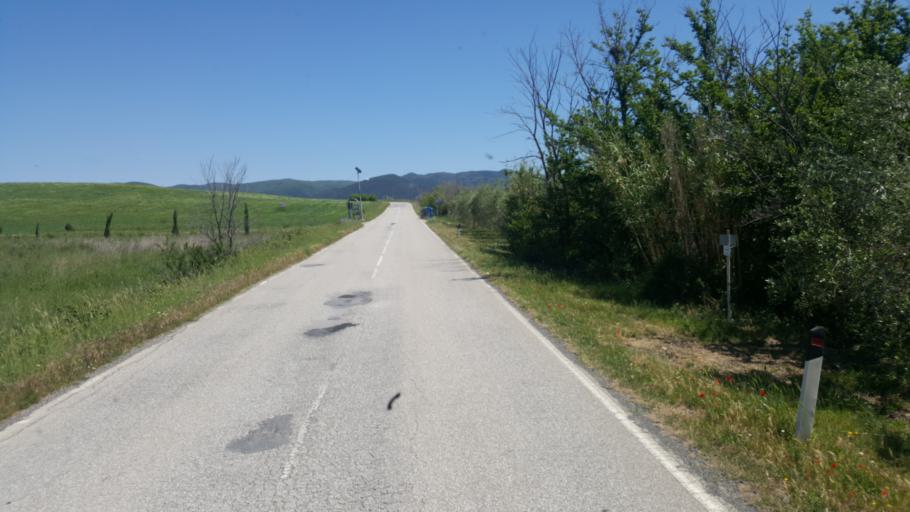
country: IT
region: Tuscany
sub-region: Provincia di Livorno
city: Rosignano Marittimo
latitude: 43.4159
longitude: 10.5179
